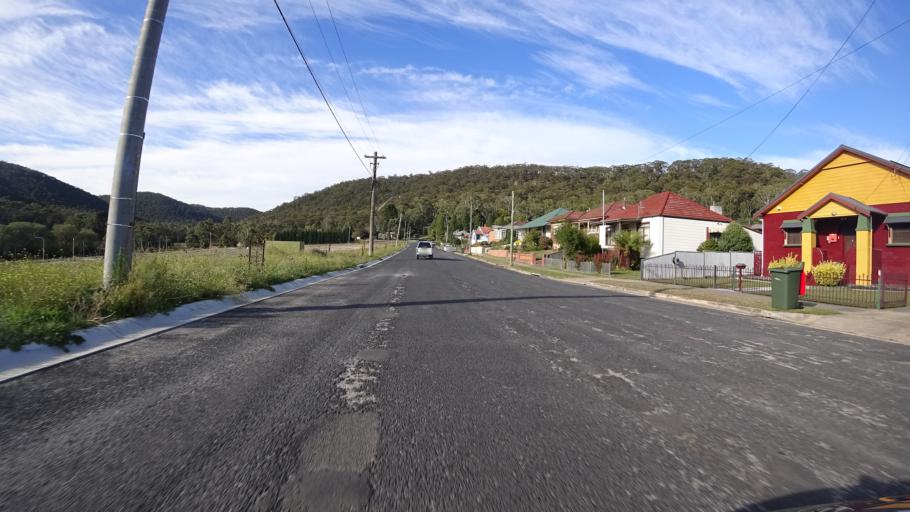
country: AU
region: New South Wales
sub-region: Lithgow
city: Lithgow
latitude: -33.4913
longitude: 150.1506
